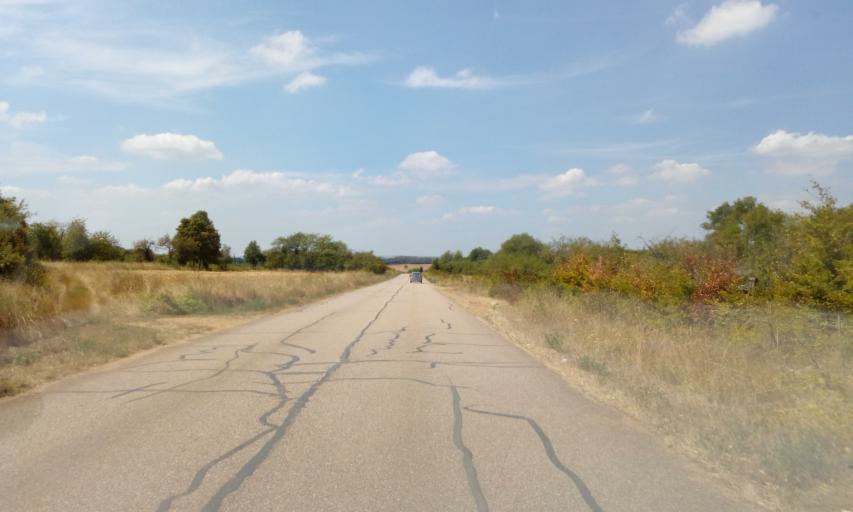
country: FR
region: Lorraine
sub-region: Departement de Meurthe-et-Moselle
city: Pagny-sur-Moselle
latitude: 48.9536
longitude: 5.8834
